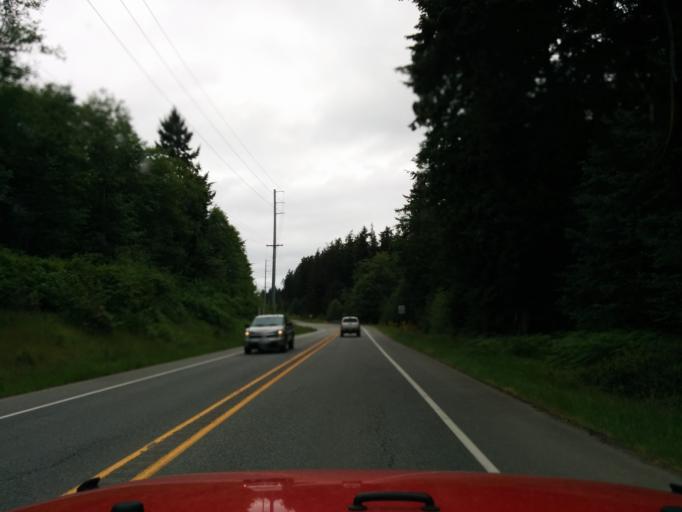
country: US
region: Washington
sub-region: Island County
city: Freeland
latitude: 48.0700
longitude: -122.5667
